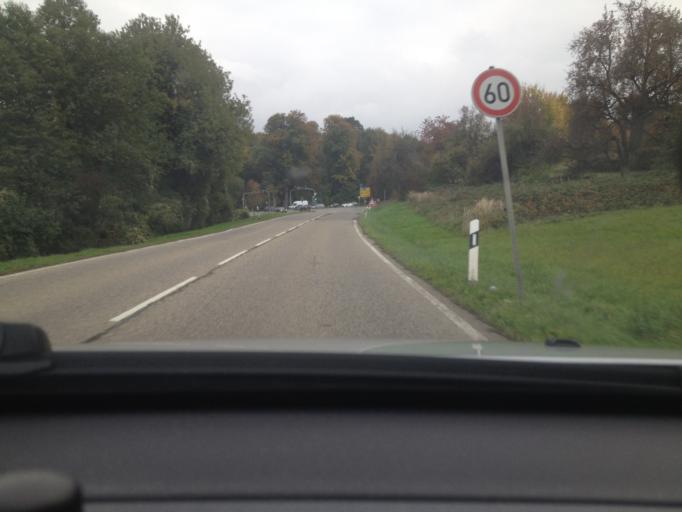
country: DE
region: Baden-Wuerttemberg
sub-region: Karlsruhe Region
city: Ispringen
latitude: 48.9144
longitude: 8.6280
